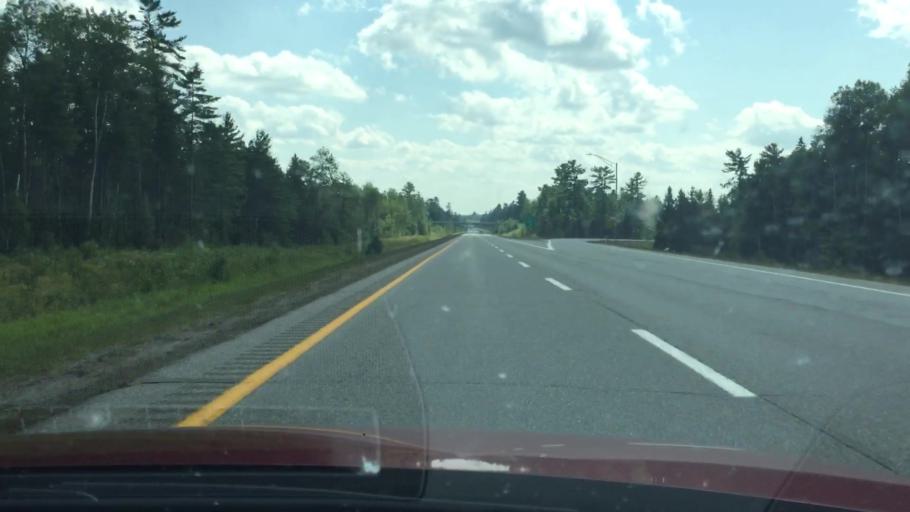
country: US
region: Maine
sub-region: Penobscot County
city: Lincoln
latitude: 45.3809
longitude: -68.6054
